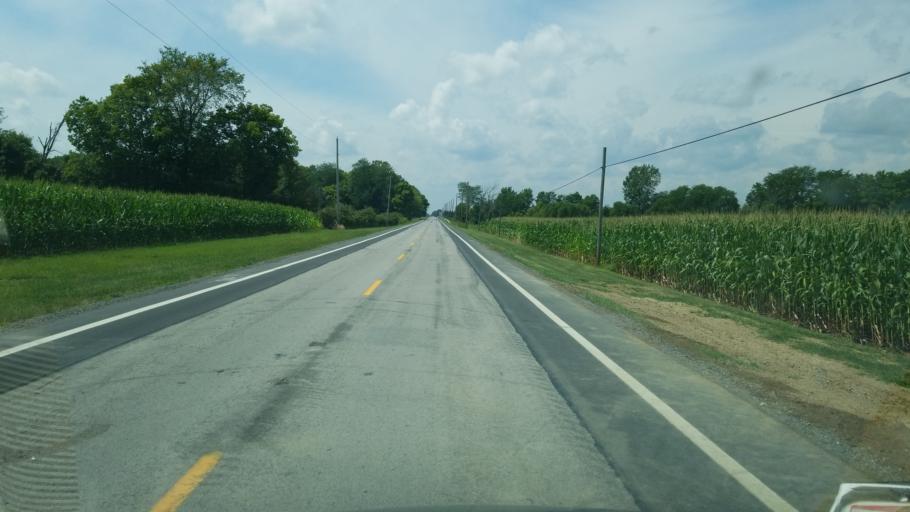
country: US
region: Ohio
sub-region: Hancock County
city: Arlington
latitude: 40.8924
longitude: -83.6762
